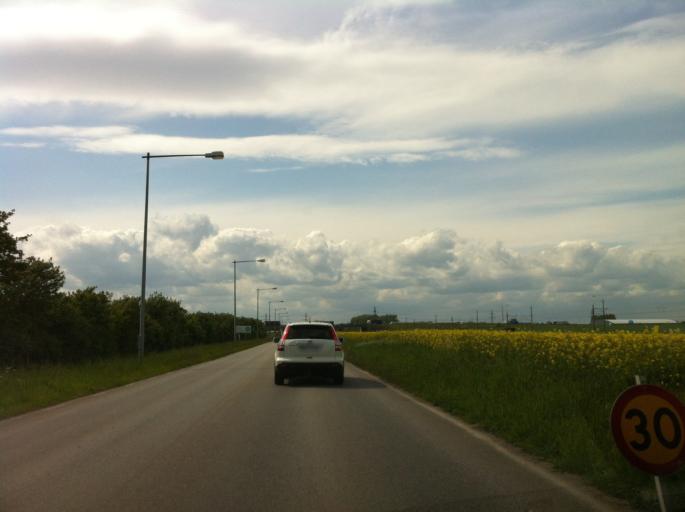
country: SE
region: Skane
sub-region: Landskrona
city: Asmundtorp
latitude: 55.8634
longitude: 12.8878
